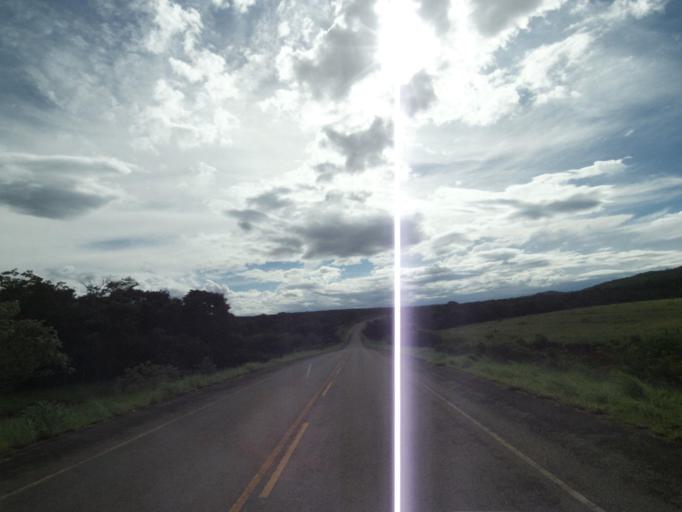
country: BR
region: Goias
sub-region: Jaragua
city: Jaragua
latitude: -15.8388
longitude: -49.2844
